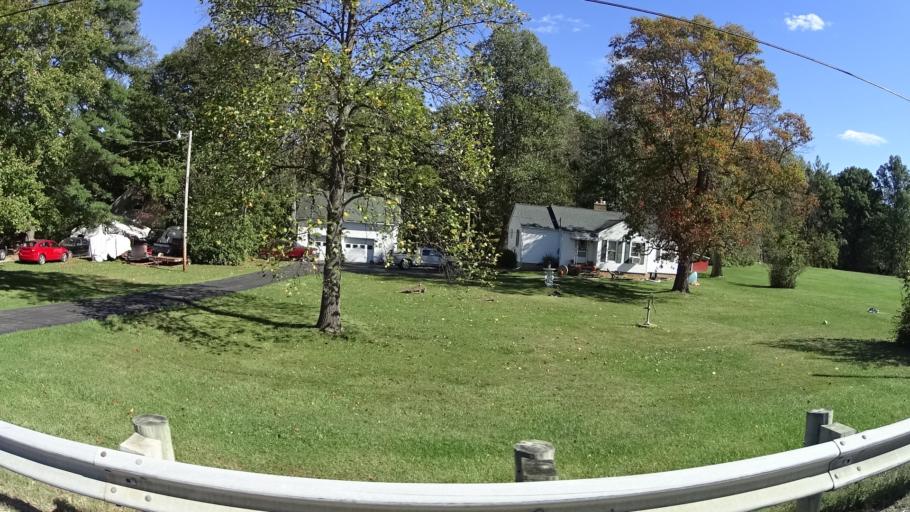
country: US
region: Ohio
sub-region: Lorain County
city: Grafton
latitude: 41.2860
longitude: -82.0820
